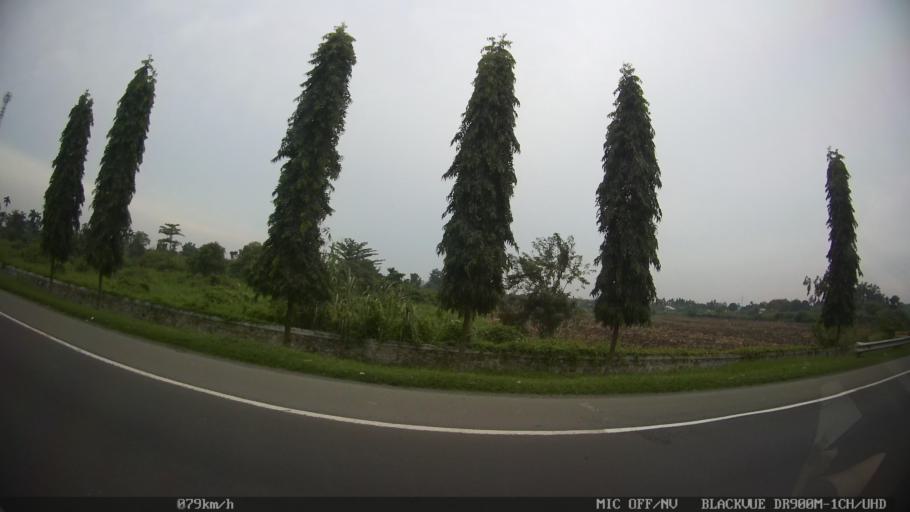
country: ID
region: North Sumatra
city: Medan
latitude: 3.5609
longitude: 98.7256
